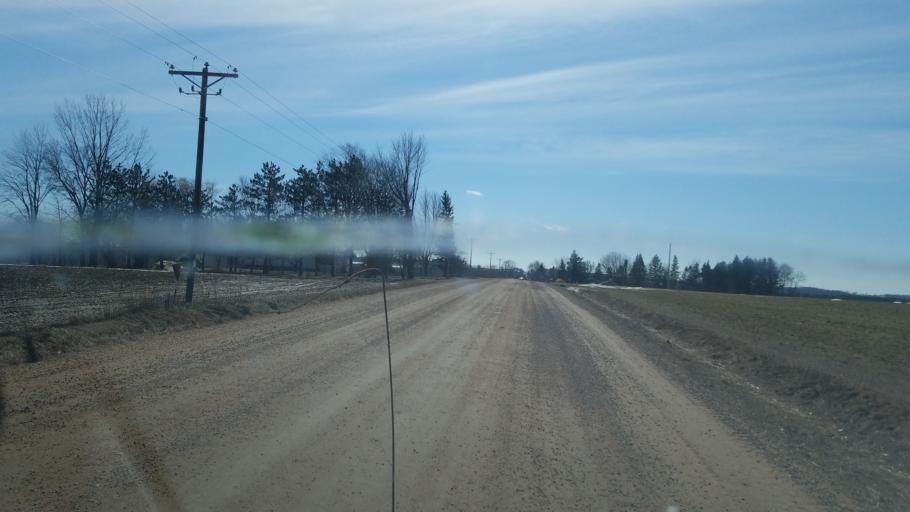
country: US
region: Wisconsin
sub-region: Clark County
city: Loyal
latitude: 44.6062
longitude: -90.4565
